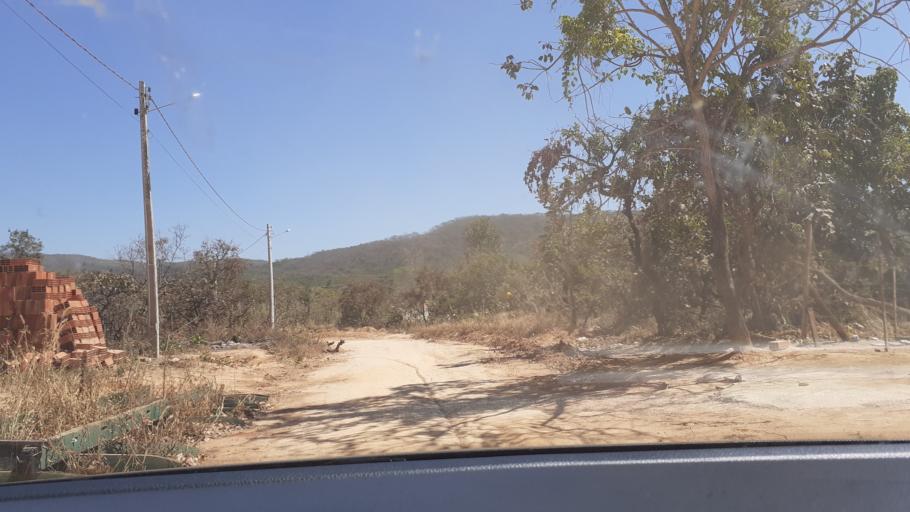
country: BR
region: Goias
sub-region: Caldas Novas
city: Caldas Novas
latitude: -17.7413
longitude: -48.6508
